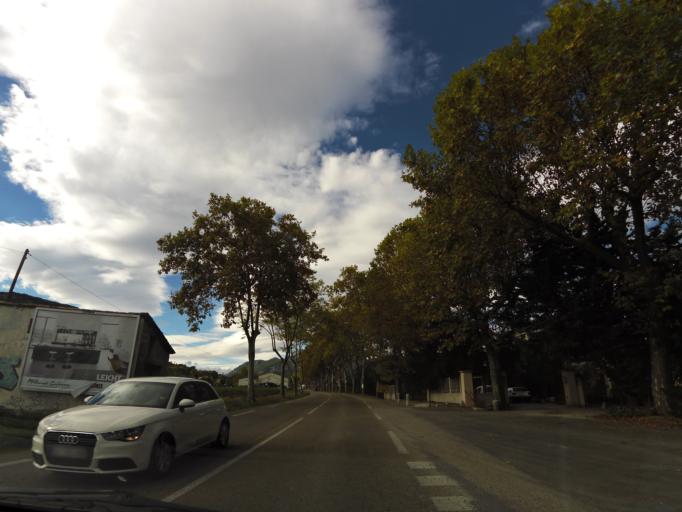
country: FR
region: Languedoc-Roussillon
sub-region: Departement du Gard
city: Saint-Hippolyte-du-Fort
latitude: 43.9565
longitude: 3.8672
